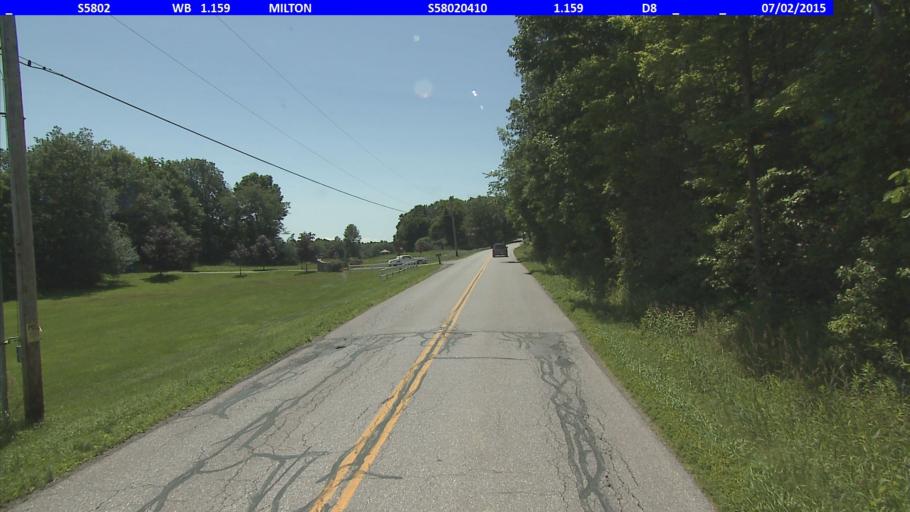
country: US
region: Vermont
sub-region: Chittenden County
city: Milton
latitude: 44.6238
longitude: -73.1988
